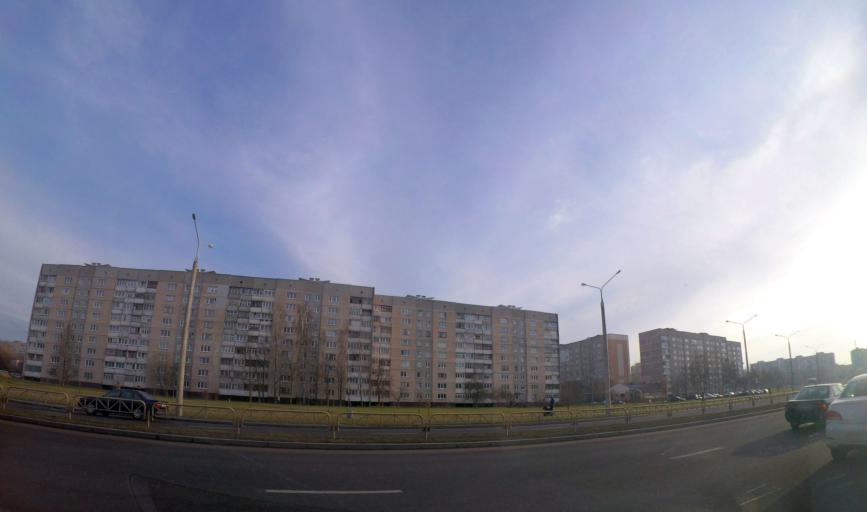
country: BY
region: Grodnenskaya
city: Hrodna
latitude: 53.6601
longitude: 23.7820
